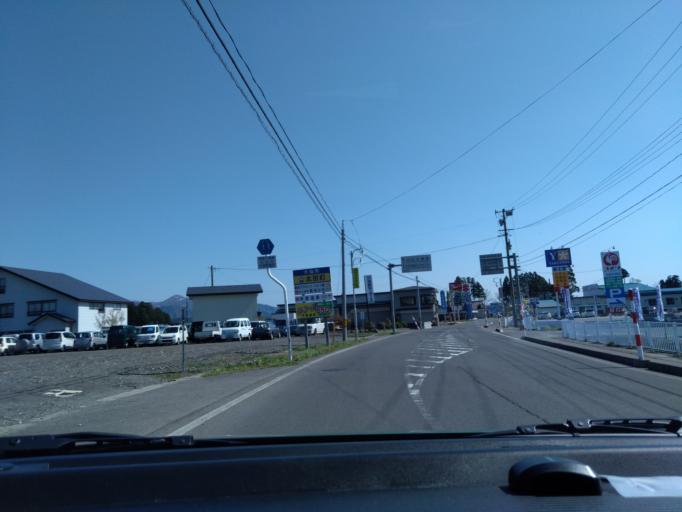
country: JP
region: Akita
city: Kakunodatemachi
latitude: 39.5072
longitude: 140.5960
